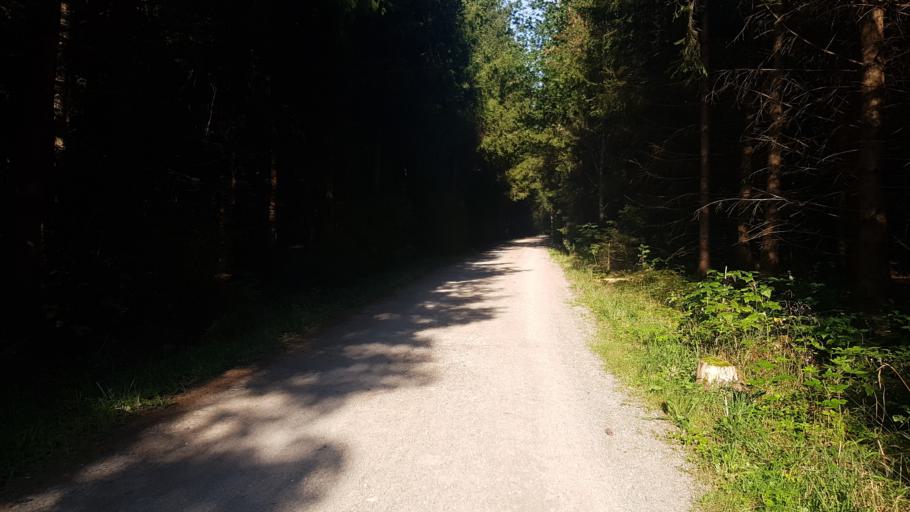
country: DE
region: Bavaria
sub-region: Upper Bavaria
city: Gauting
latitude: 48.0898
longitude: 11.3574
